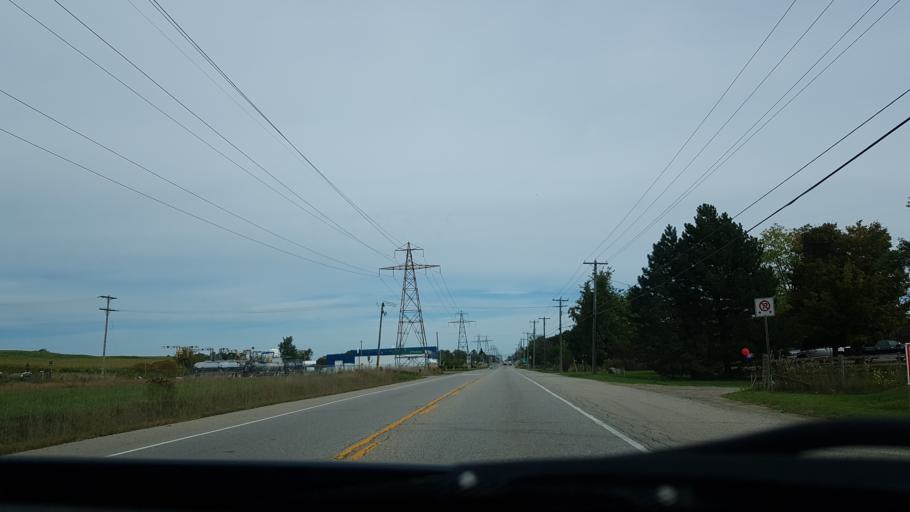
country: CA
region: Ontario
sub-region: Wellington County
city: Guelph
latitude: 43.4842
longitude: -80.2918
